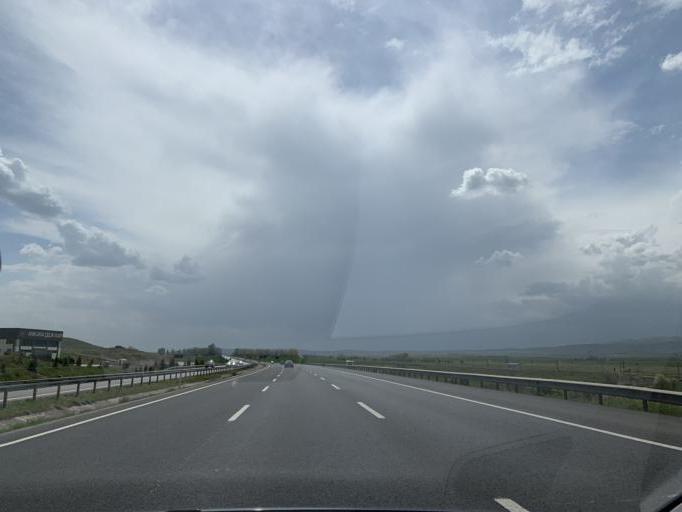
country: TR
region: Ankara
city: Temelli
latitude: 39.7018
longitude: 32.2709
